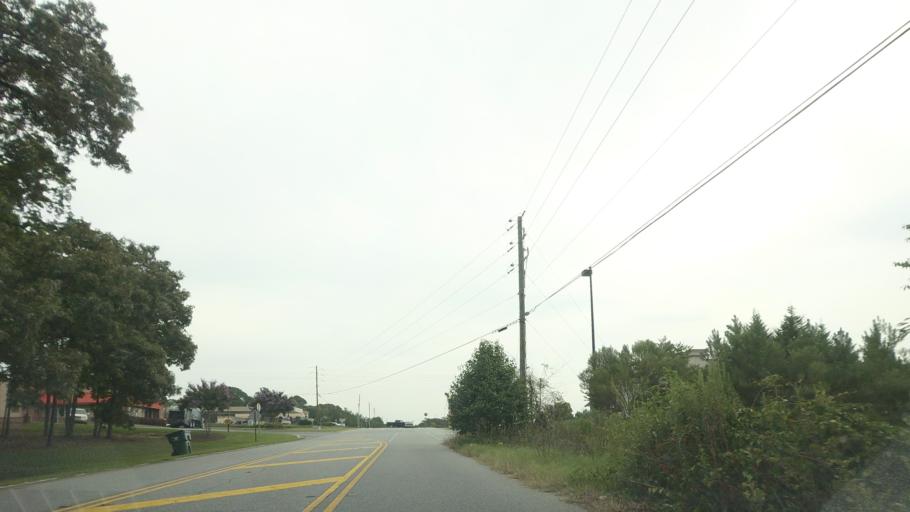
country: US
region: Georgia
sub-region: Houston County
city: Warner Robins
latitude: 32.5925
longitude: -83.6149
